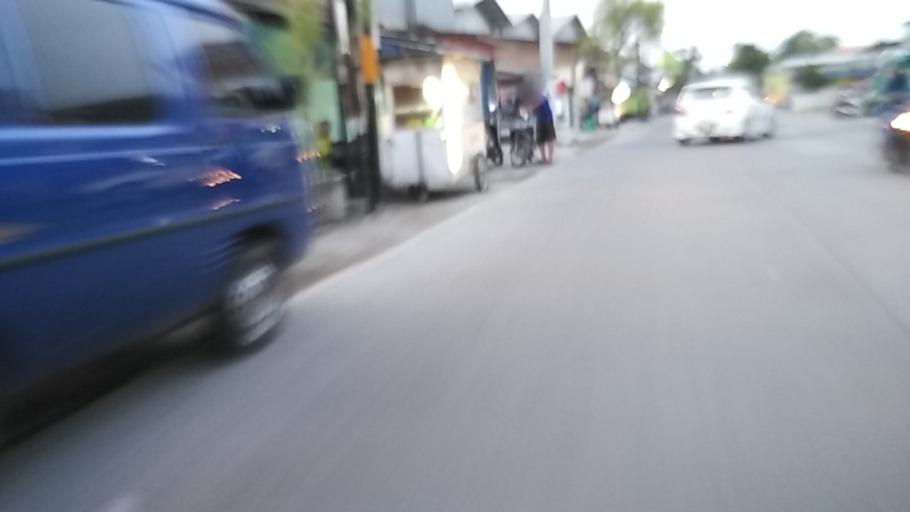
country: ID
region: Central Java
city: Semarang
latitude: -6.9821
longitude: 110.4536
